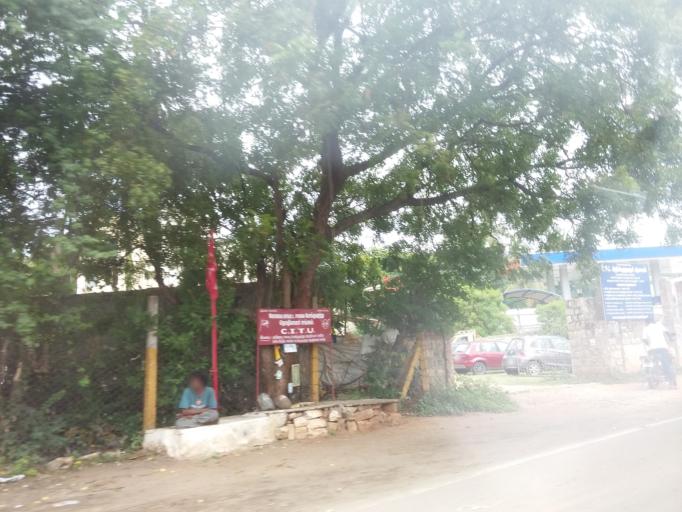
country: IN
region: Tamil Nadu
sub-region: Coimbatore
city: Perur
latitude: 11.0206
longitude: 76.9185
